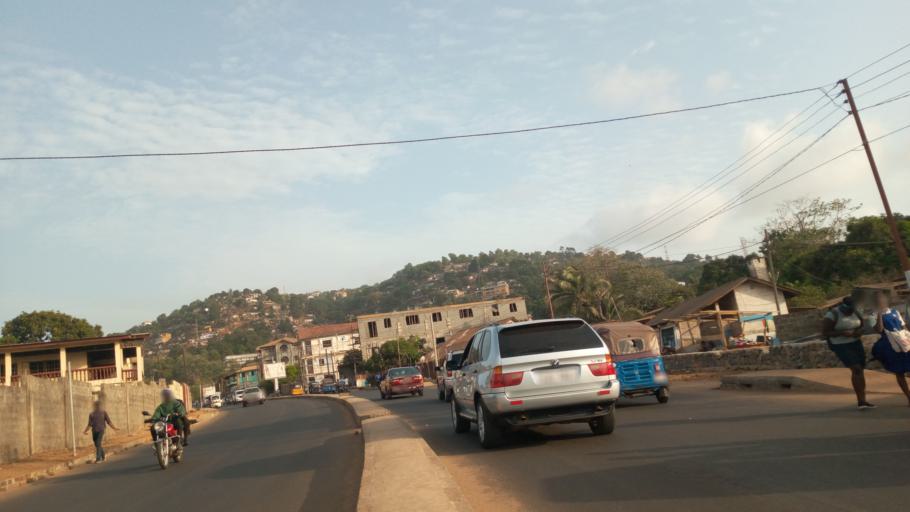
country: SL
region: Western Area
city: Freetown
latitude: 8.4725
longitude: -13.2481
